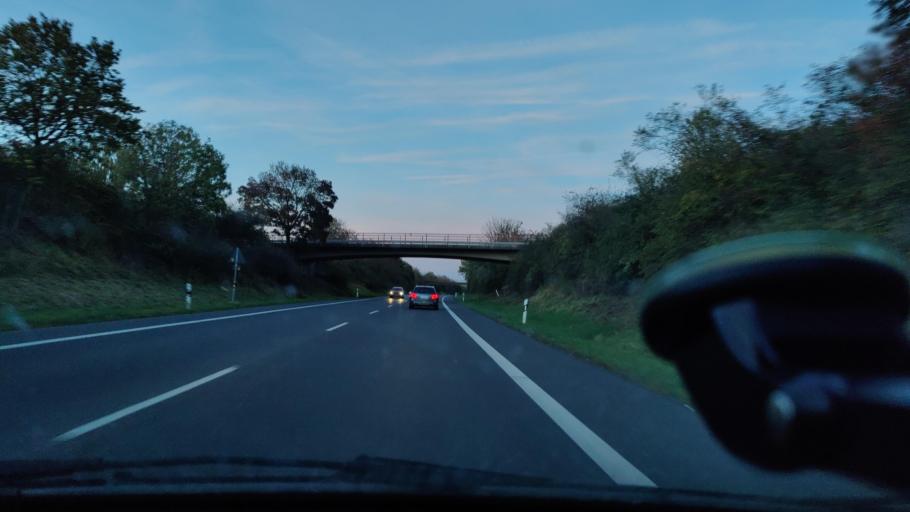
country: DE
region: North Rhine-Westphalia
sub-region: Regierungsbezirk Koln
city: Heinsberg
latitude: 51.0524
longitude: 6.1047
